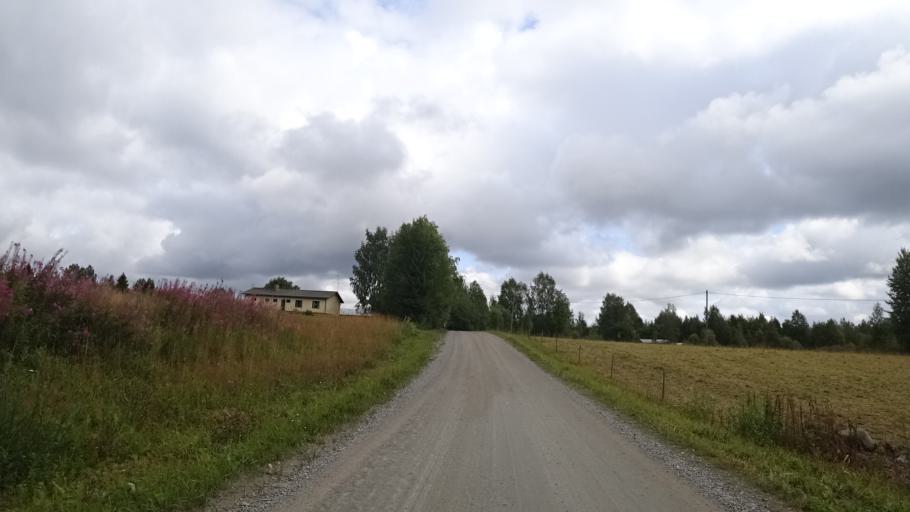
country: FI
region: North Karelia
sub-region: Joensuu
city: Ilomantsi
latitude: 62.9334
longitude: 31.2925
